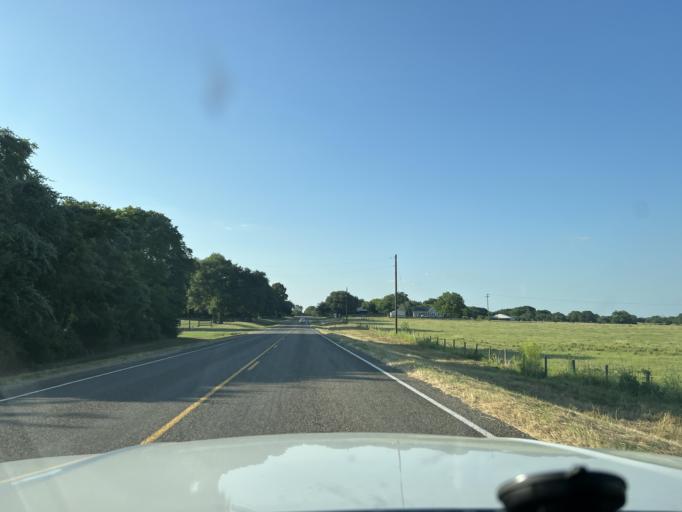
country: US
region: Texas
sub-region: Washington County
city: Brenham
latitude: 30.1998
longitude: -96.3939
